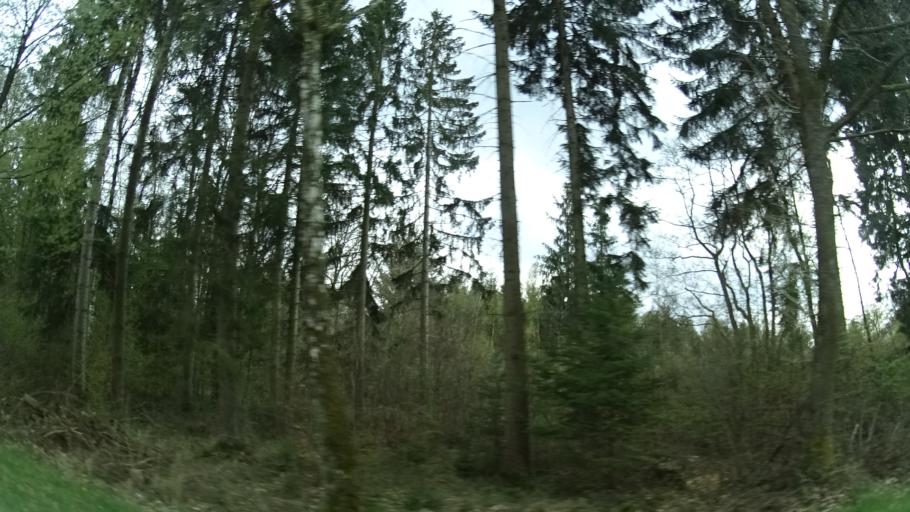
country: DE
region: Rheinland-Pfalz
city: Seesbach
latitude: 49.8674
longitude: 7.5701
